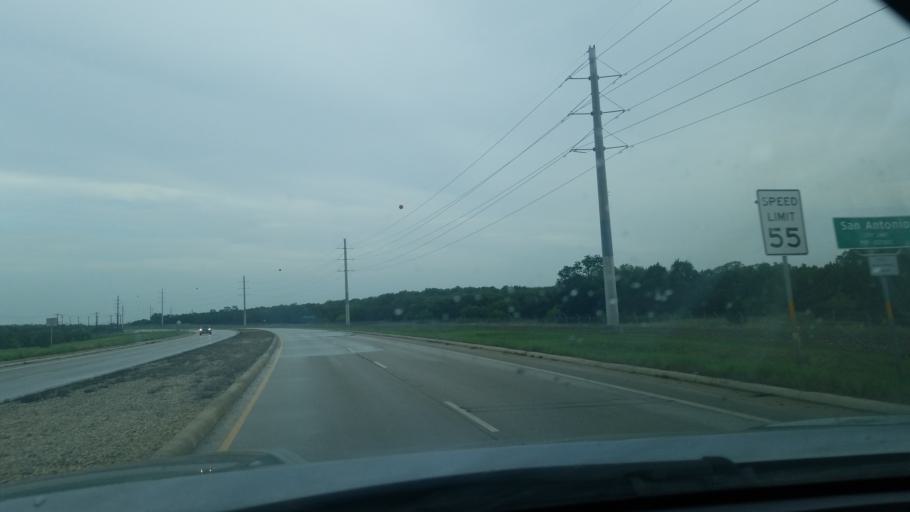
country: US
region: Texas
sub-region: Bexar County
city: Timberwood Park
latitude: 29.6568
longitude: -98.5212
